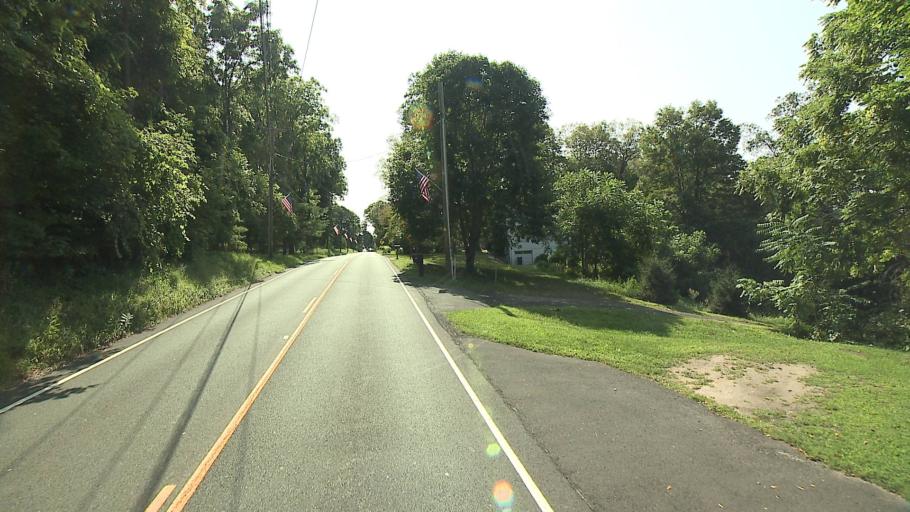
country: US
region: Connecticut
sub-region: Fairfield County
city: Danbury
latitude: 41.4782
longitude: -73.4009
